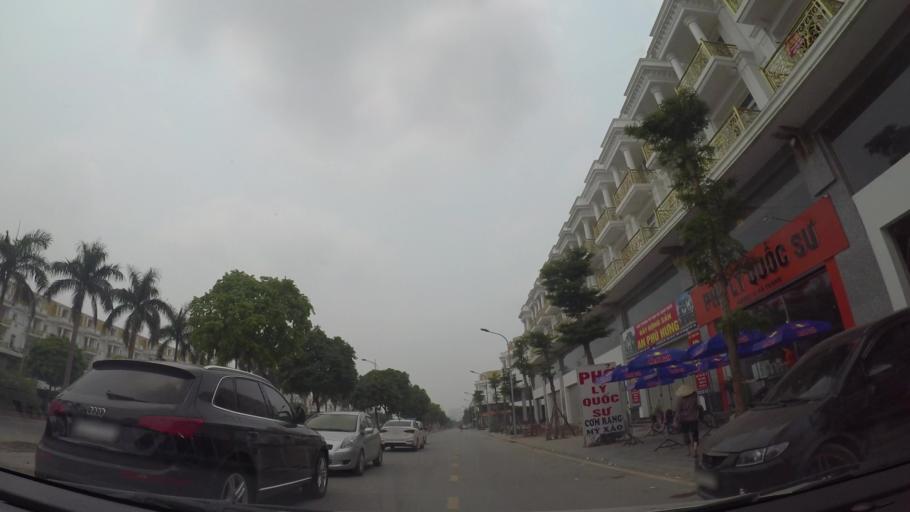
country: VN
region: Ha Noi
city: Ha Dong
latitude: 20.9854
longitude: 105.7399
